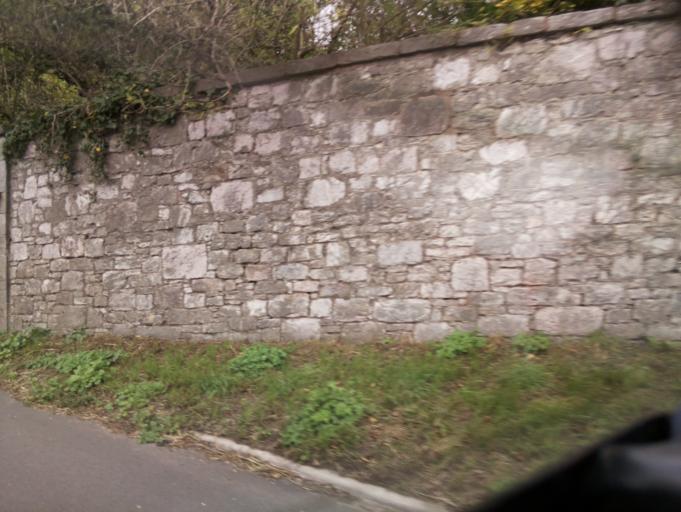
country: GB
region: England
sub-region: Devon
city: Starcross
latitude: 50.6323
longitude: -3.4508
